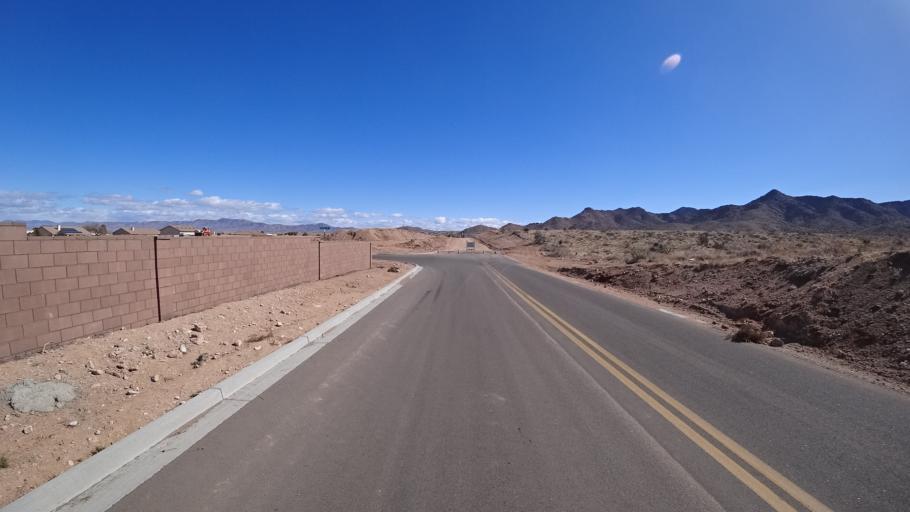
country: US
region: Arizona
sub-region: Mohave County
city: Kingman
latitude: 35.1959
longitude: -113.9621
